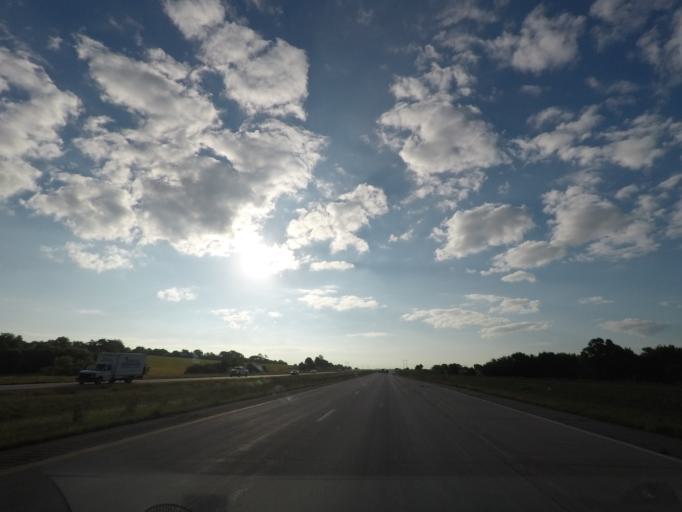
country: US
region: Iowa
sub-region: Warren County
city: Norwalk
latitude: 41.5059
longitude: -93.6416
